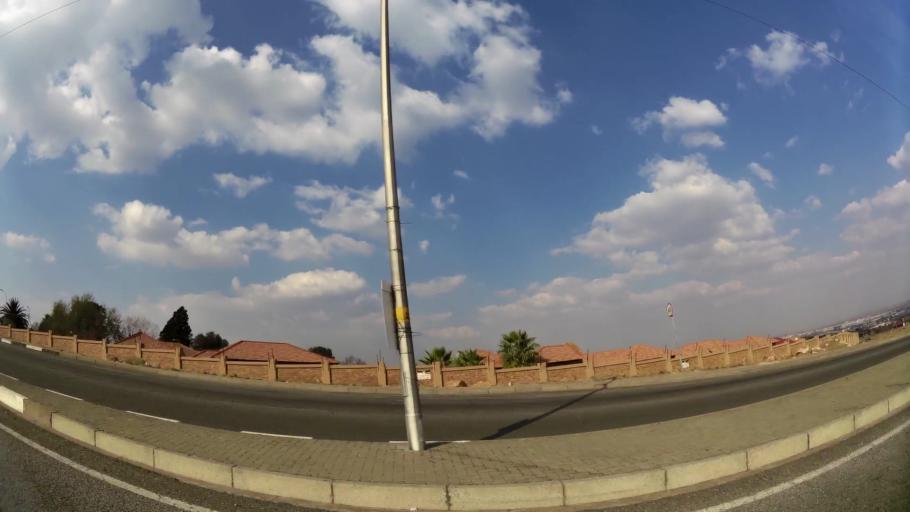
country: ZA
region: Gauteng
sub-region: Ekurhuleni Metropolitan Municipality
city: Germiston
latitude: -26.2446
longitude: 28.1650
